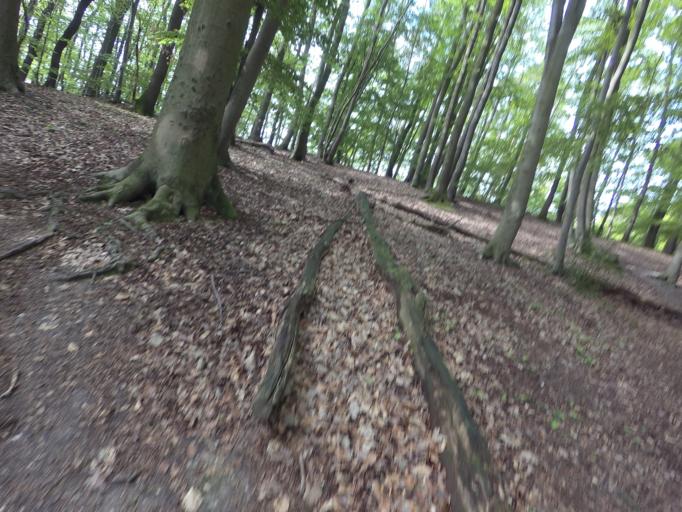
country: NL
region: Limburg
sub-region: Gemeente Kerkrade
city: Kerkrade
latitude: 50.8984
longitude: 6.0310
